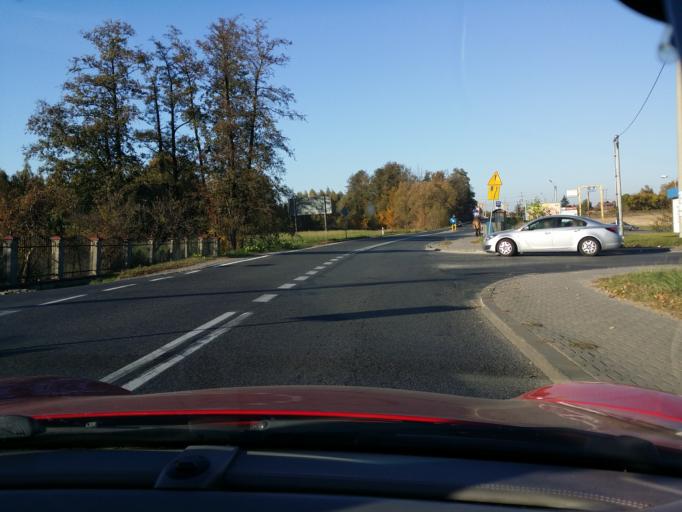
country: PL
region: Masovian Voivodeship
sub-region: Powiat radomski
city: Trablice
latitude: 51.3524
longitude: 21.1288
